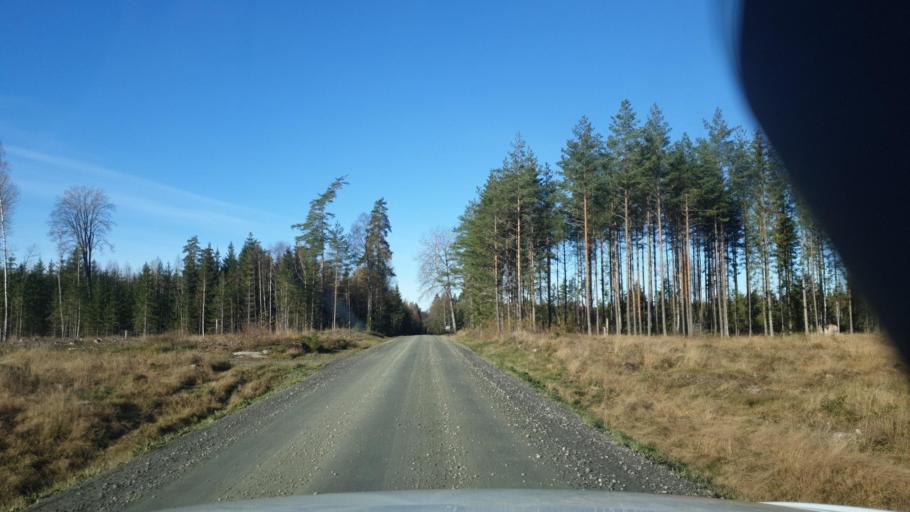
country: SE
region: Vaermland
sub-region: Karlstads Kommun
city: Valberg
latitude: 59.4485
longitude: 13.1107
